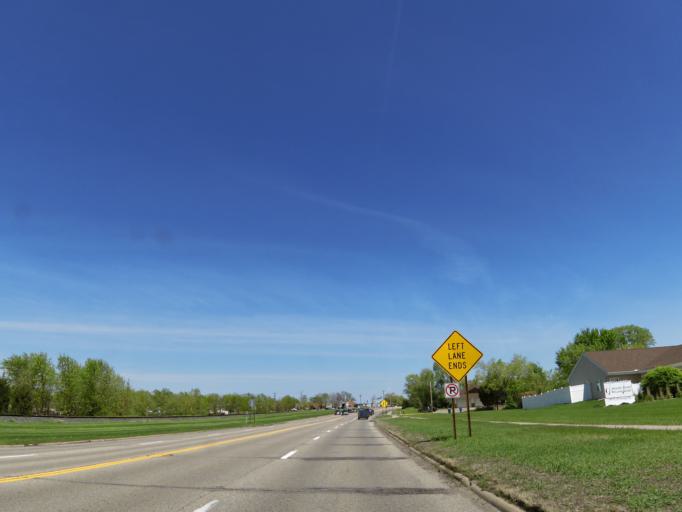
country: US
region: Minnesota
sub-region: Hennepin County
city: Bloomington
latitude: 44.8242
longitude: -93.3015
